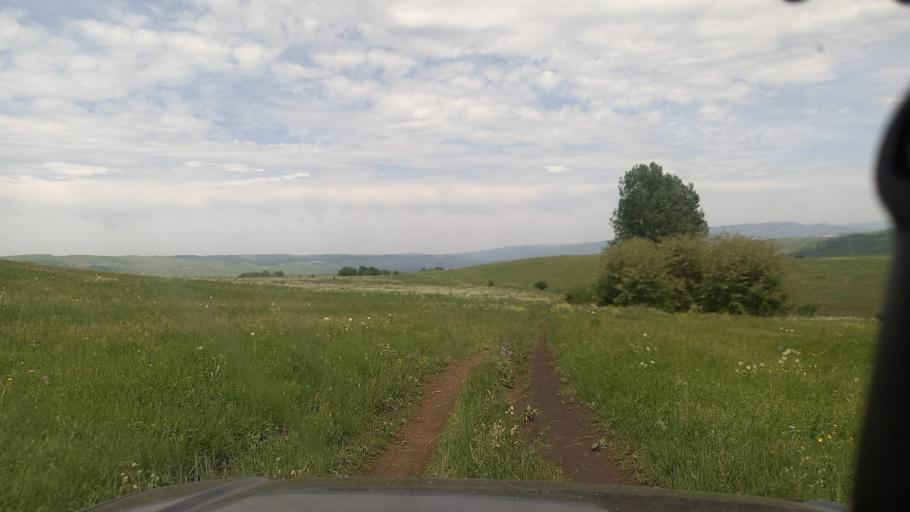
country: RU
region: Krasnodarskiy
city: Peredovaya
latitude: 44.0694
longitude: 41.3149
